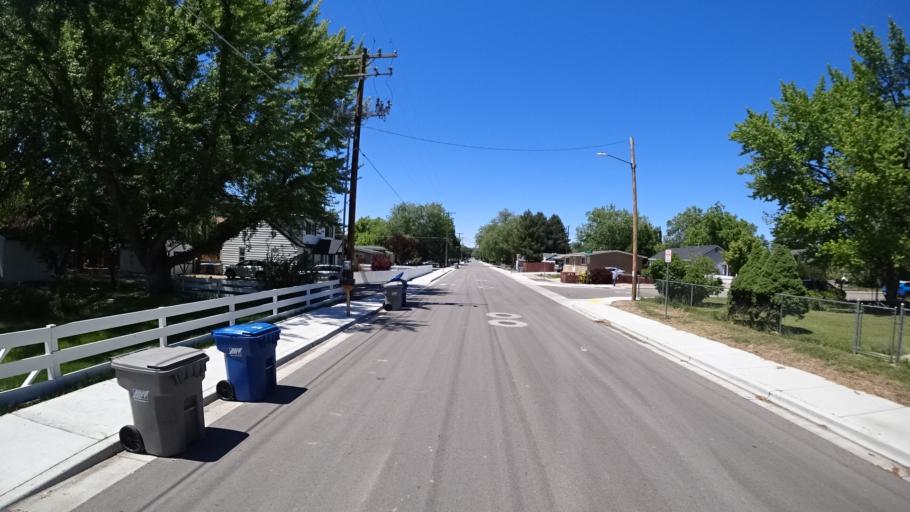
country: US
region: Idaho
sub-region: Ada County
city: Boise
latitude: 43.5826
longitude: -116.2196
